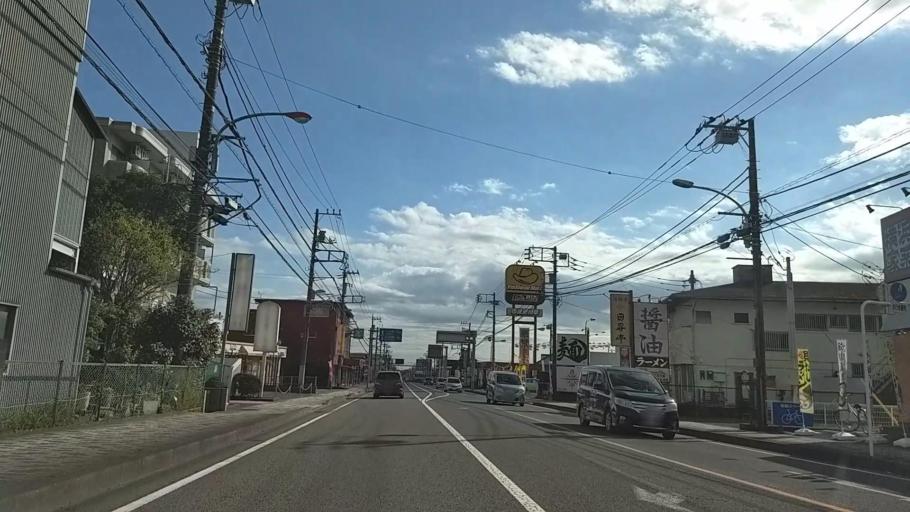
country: JP
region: Kanagawa
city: Hadano
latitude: 35.3370
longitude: 139.1531
